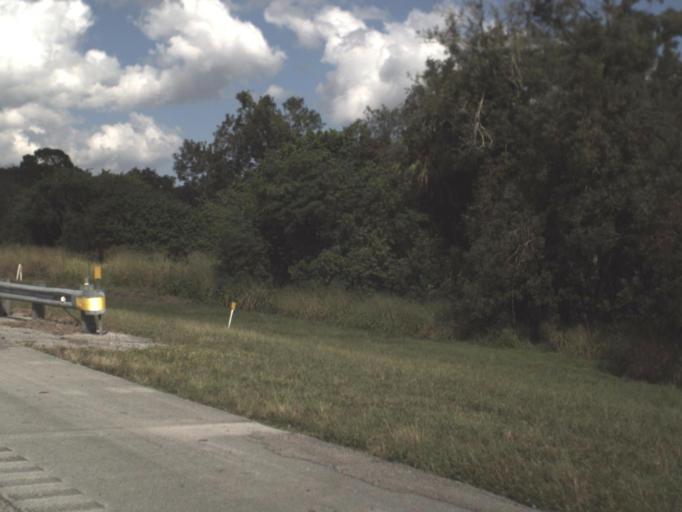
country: US
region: Florida
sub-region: Saint Lucie County
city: Fort Pierce South
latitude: 27.4017
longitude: -80.3973
